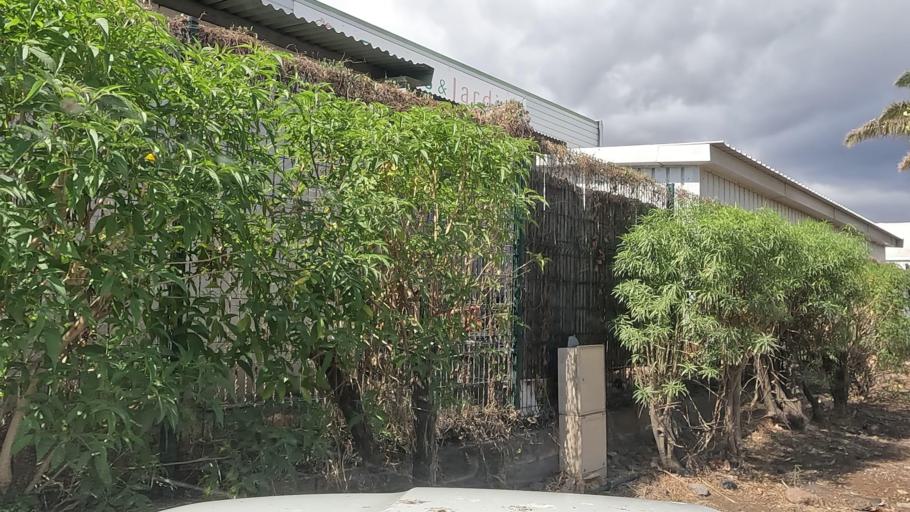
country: RE
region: Reunion
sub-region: Reunion
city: Saint-Louis
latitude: -21.2932
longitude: 55.4067
